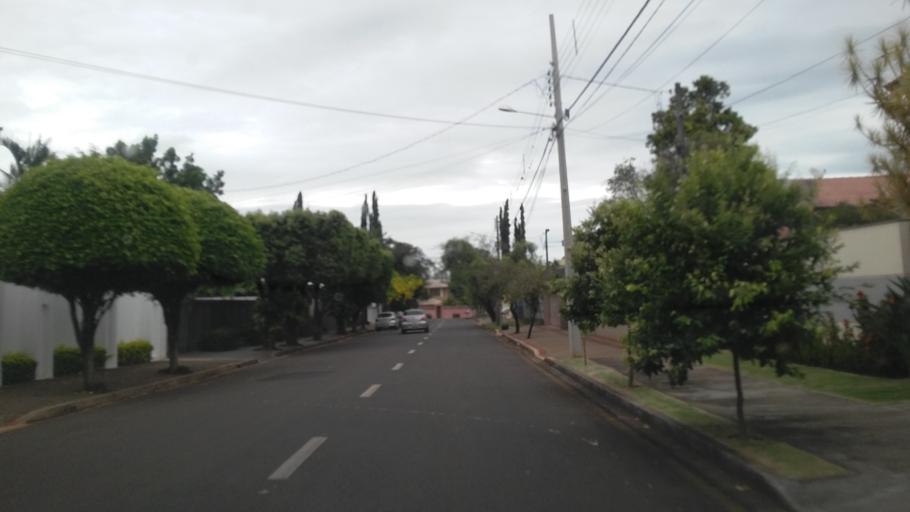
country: BR
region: Parana
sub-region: Londrina
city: Londrina
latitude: -23.3123
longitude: -51.1788
